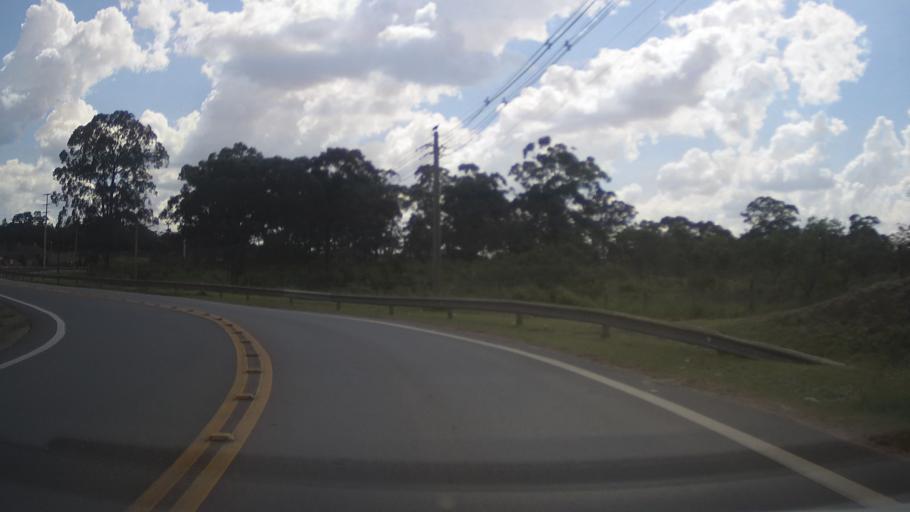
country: BR
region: Sao Paulo
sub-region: Jundiai
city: Jundiai
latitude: -23.1524
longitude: -46.8792
